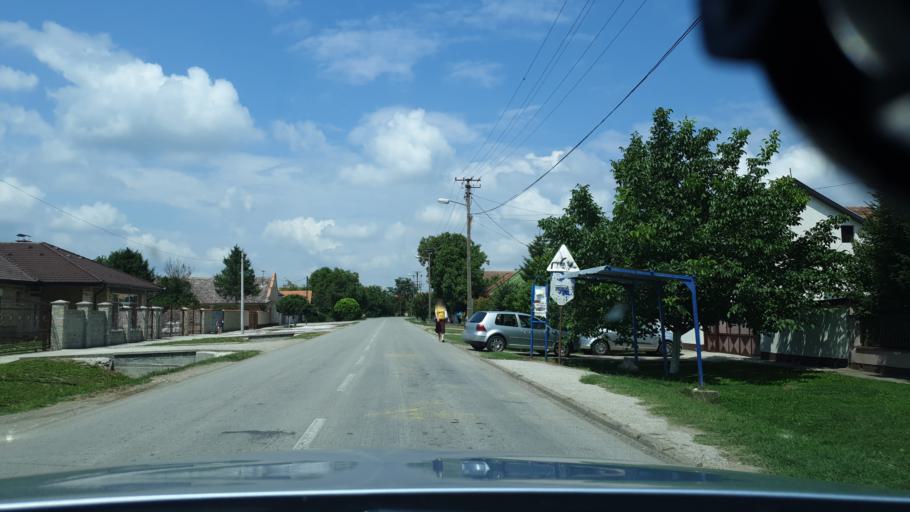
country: RS
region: Autonomna Pokrajina Vojvodina
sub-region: Juznobacki Okrug
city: Kovilj
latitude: 45.2376
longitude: 20.0285
